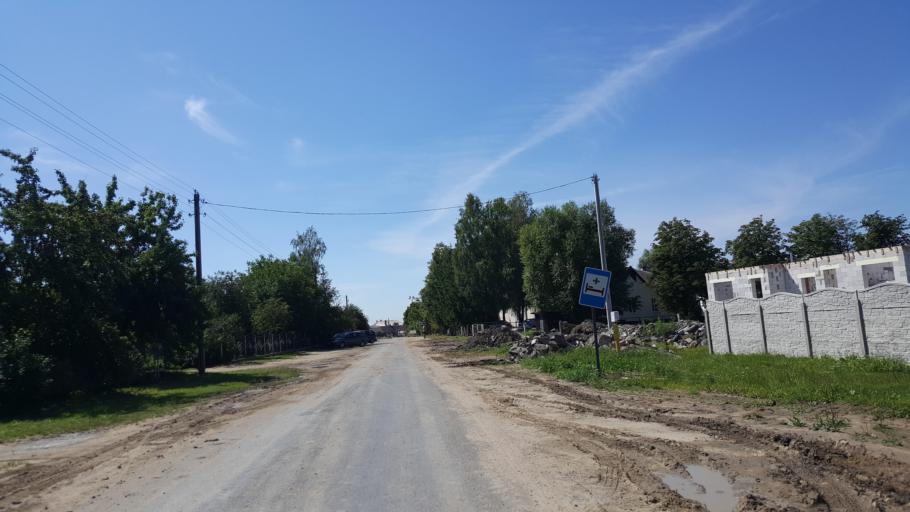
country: BY
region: Brest
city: Charnawchytsy
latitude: 52.2271
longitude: 23.7398
